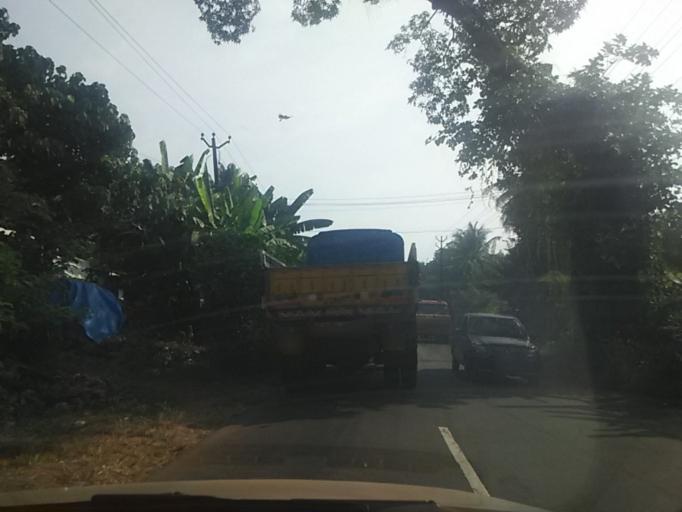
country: IN
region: Kerala
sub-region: Kozhikode
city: Kunnamangalam
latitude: 11.3120
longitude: 75.9181
